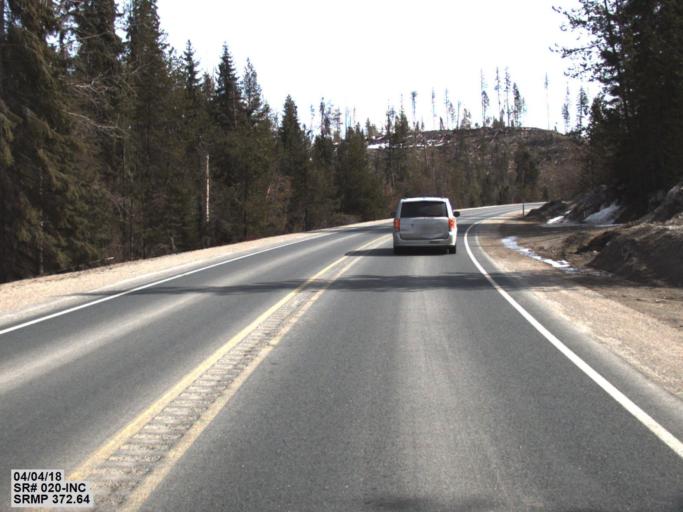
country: US
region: Washington
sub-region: Stevens County
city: Chewelah
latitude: 48.5397
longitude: -117.6009
